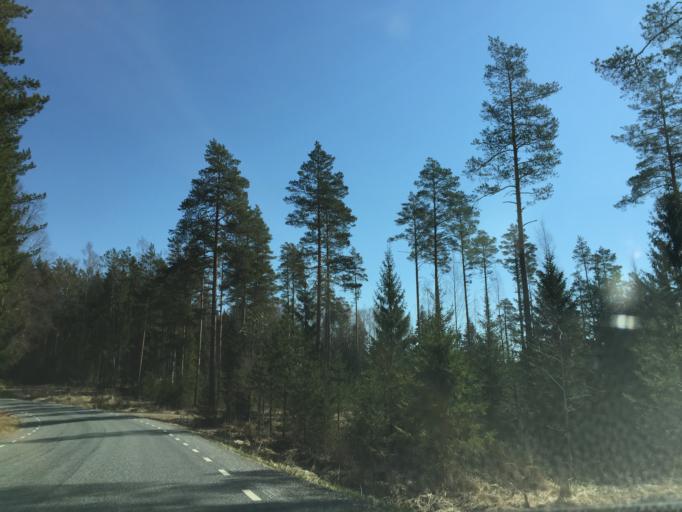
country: EE
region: Tartu
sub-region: Alatskivi vald
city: Kallaste
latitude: 58.5783
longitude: 27.0194
